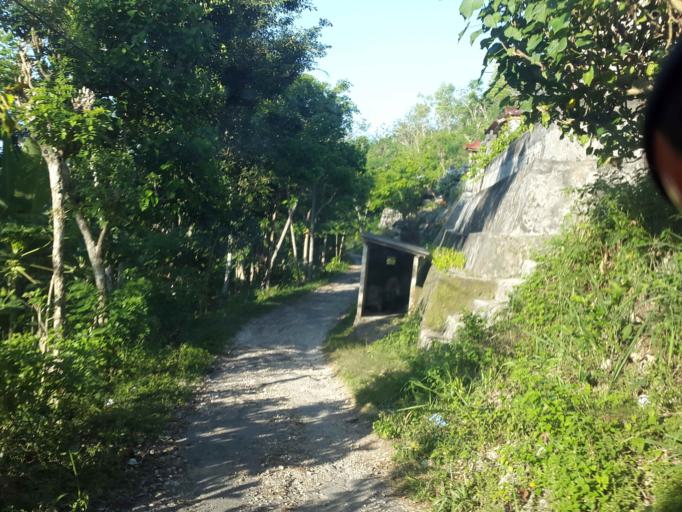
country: ID
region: Bali
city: Pejukutan
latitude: -8.7374
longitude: 115.5676
